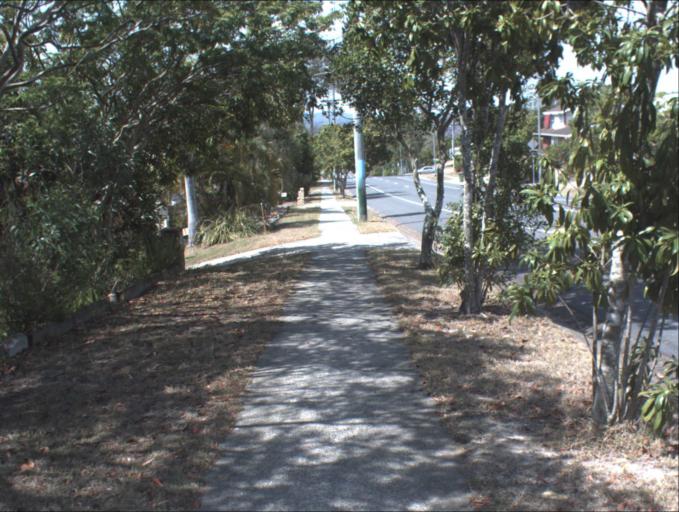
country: AU
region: Queensland
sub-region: Logan
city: Slacks Creek
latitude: -27.6588
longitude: 153.1864
